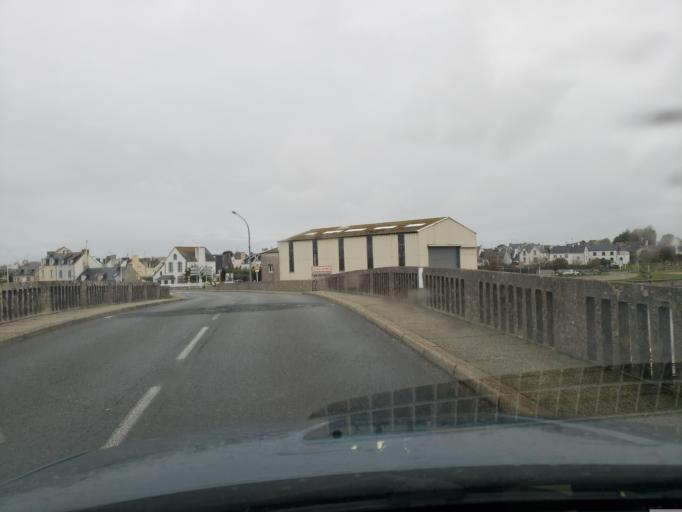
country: FR
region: Brittany
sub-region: Departement du Finistere
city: Guilvinec
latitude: 47.7970
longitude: -4.2746
